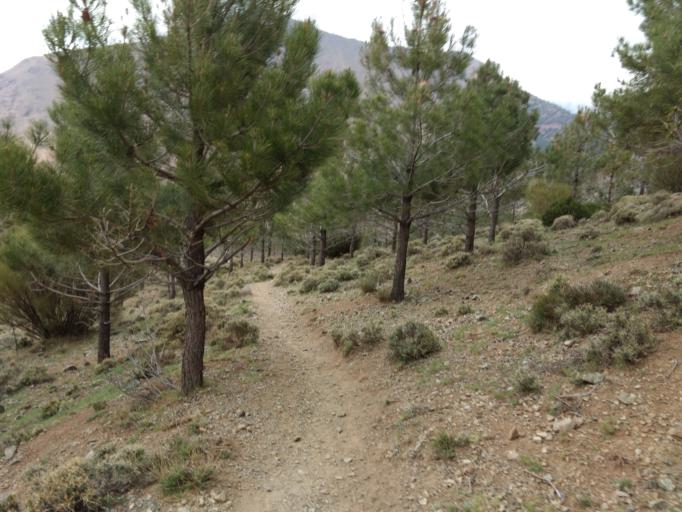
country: MA
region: Marrakech-Tensift-Al Haouz
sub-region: Al-Haouz
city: Moulay Brahim
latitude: 31.1326
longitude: -7.9083
